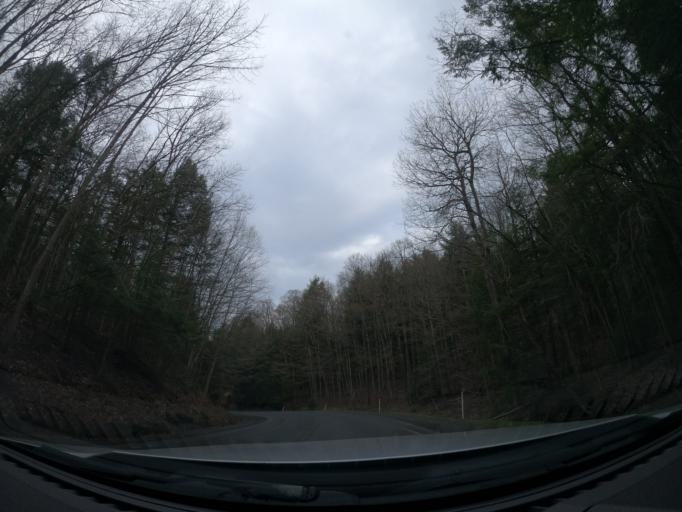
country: US
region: New York
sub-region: Madison County
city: Cazenovia
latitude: 42.8393
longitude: -75.7887
